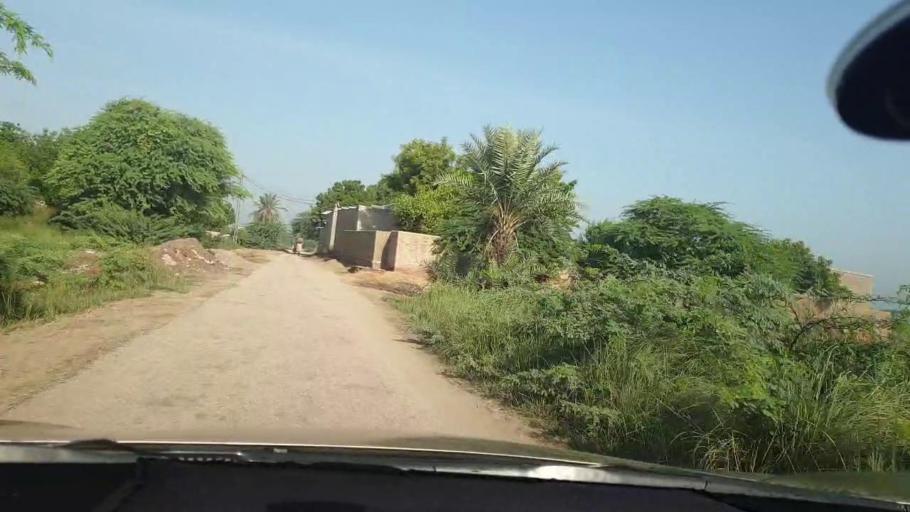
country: PK
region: Sindh
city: Kambar
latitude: 27.6537
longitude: 68.0342
